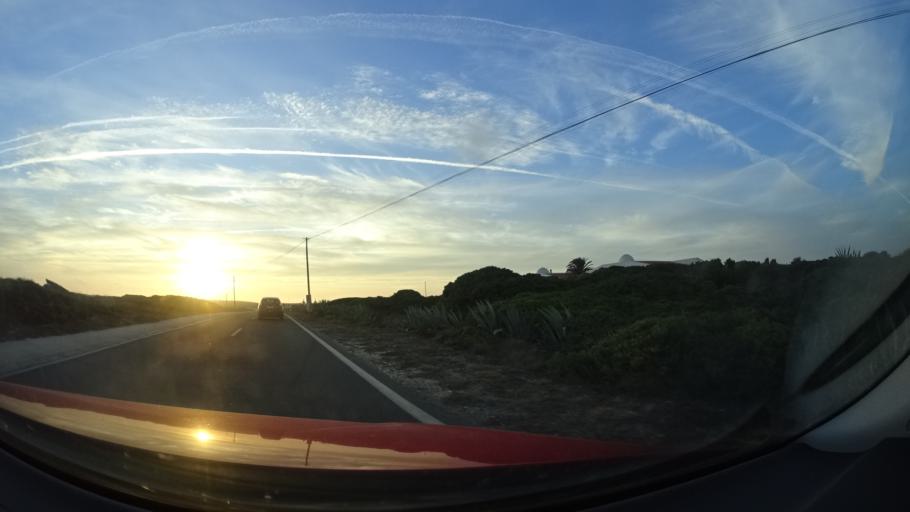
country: PT
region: Faro
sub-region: Vila do Bispo
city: Sagres
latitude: 37.0278
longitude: -8.9790
